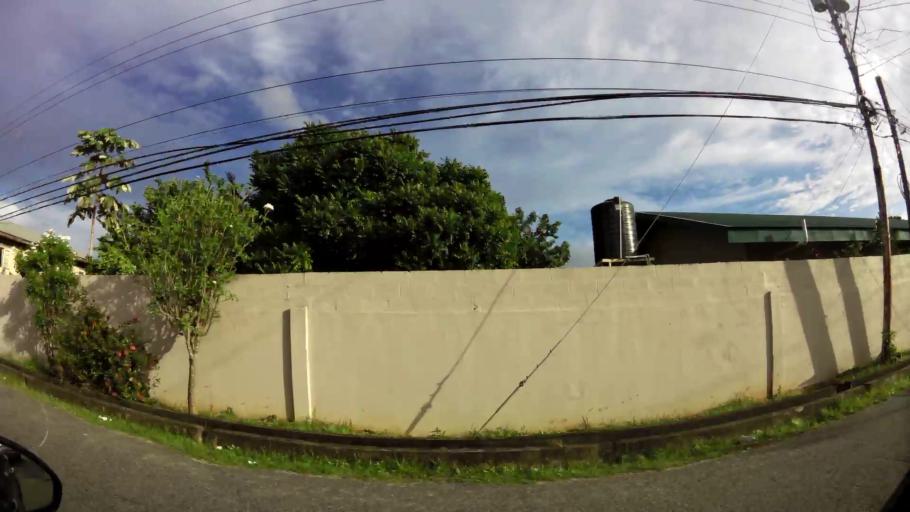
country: TT
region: Tunapuna/Piarco
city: Tunapuna
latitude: 10.6425
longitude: -61.4055
